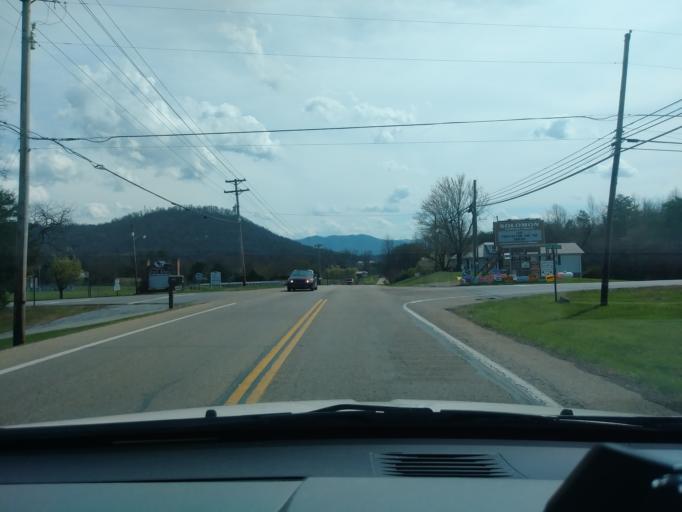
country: US
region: Tennessee
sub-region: Greene County
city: Greeneville
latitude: 36.0529
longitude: -82.8593
